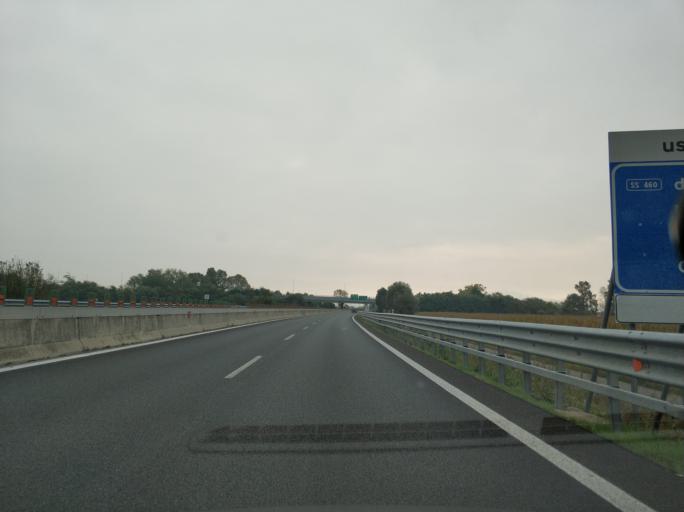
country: IT
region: Piedmont
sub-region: Provincia di Torino
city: Borgaro Torinese
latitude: 45.1719
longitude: 7.6760
